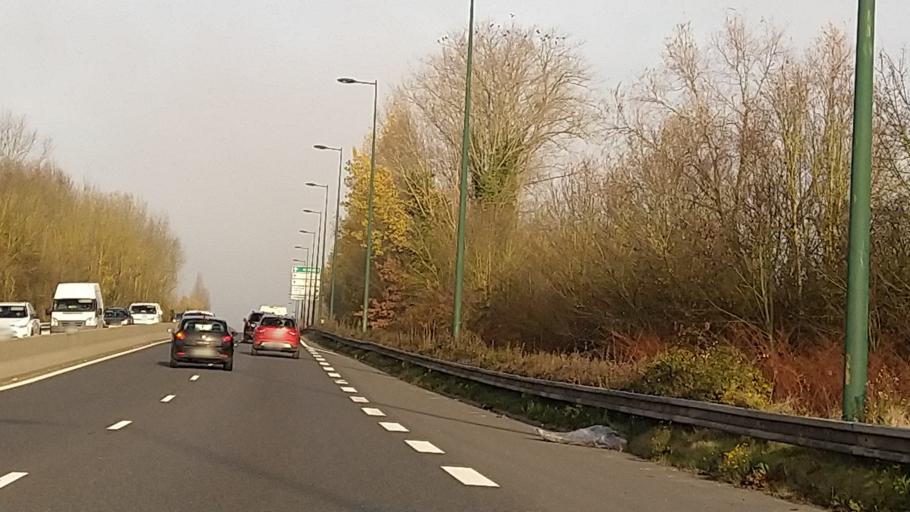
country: FR
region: Ile-de-France
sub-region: Departement du Val-d'Oise
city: Champagne-sur-Oise
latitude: 49.1363
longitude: 2.2550
